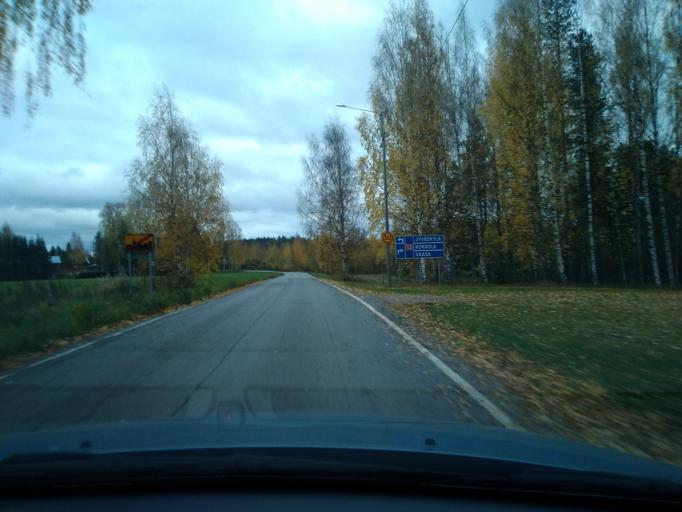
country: FI
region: Central Finland
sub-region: Saarijaervi-Viitasaari
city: Saarijaervi
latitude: 62.6895
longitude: 25.3155
